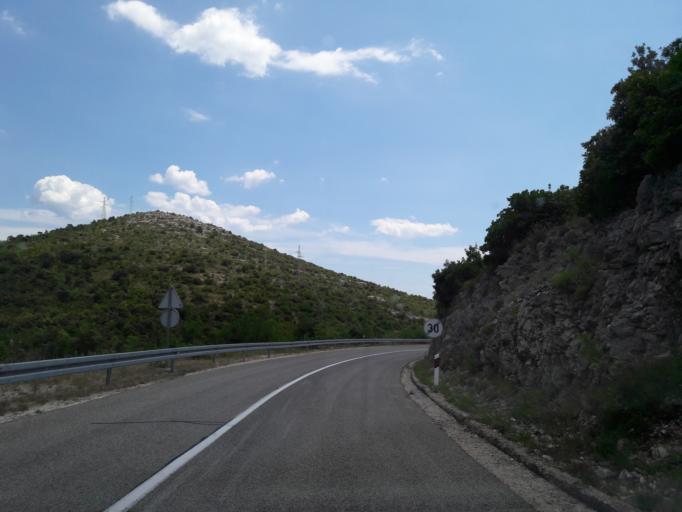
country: HR
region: Dubrovacko-Neretvanska
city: Orebic
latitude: 42.9751
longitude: 17.2671
